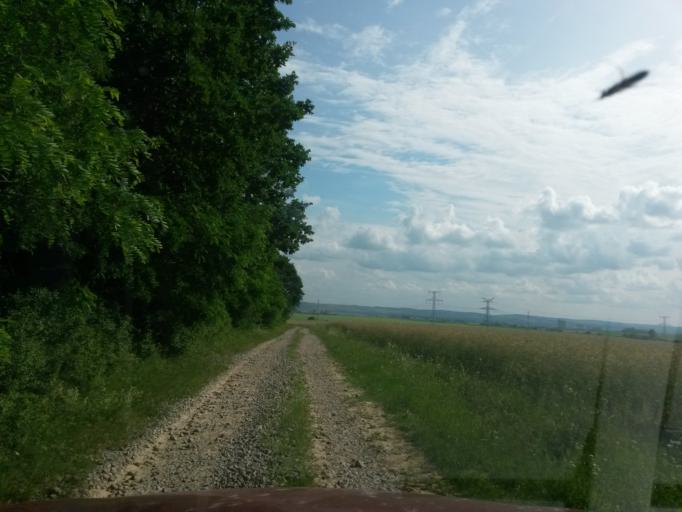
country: SK
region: Kosicky
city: Moldava nad Bodvou
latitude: 48.6111
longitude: 21.1025
